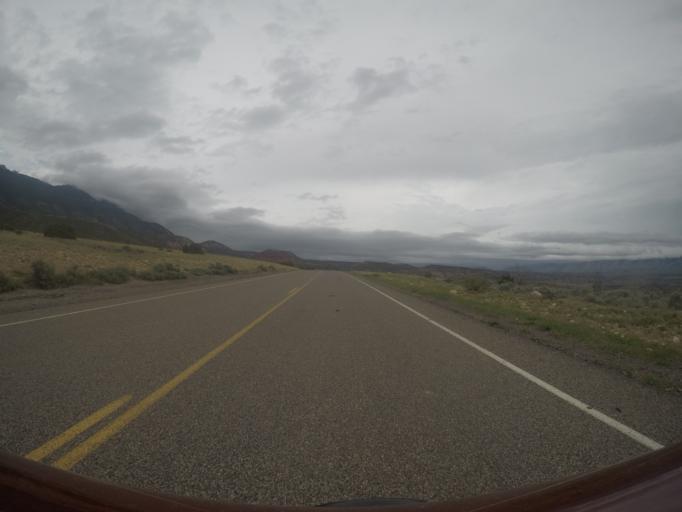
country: US
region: Wyoming
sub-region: Big Horn County
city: Lovell
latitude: 45.0929
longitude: -108.2502
